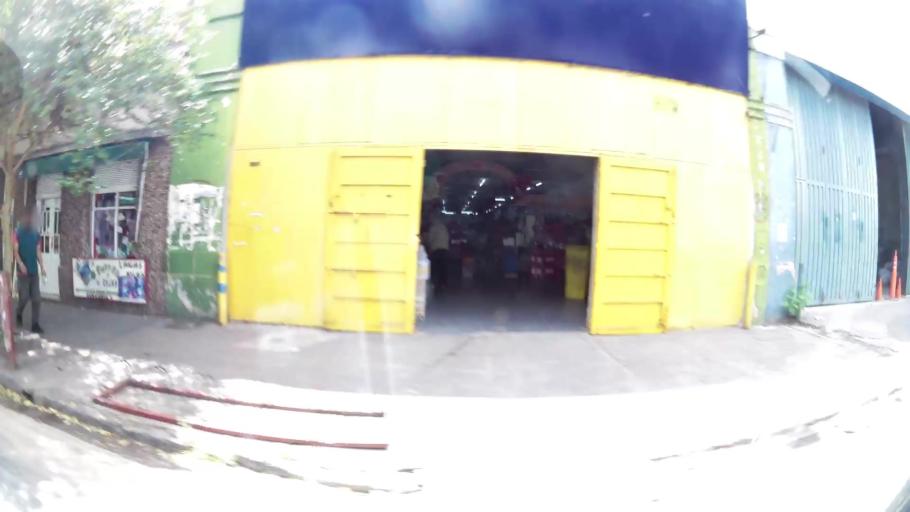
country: AR
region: Santa Fe
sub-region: Departamento de Rosario
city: Rosario
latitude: -32.9732
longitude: -60.6346
